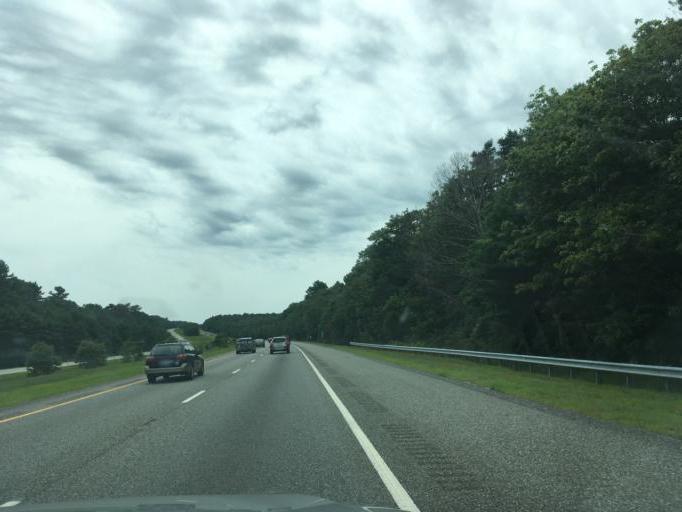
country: US
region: Rhode Island
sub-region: Kent County
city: West Greenwich
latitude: 41.6321
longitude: -71.6337
